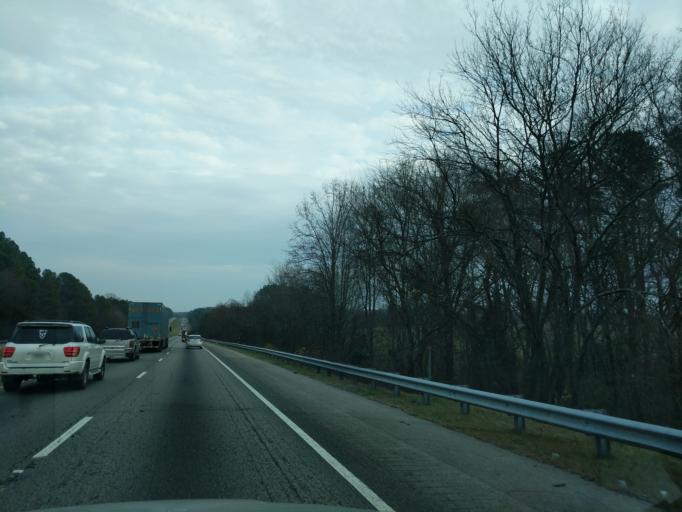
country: US
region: Georgia
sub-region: Jackson County
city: Braselton
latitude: 34.1286
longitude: -83.7075
